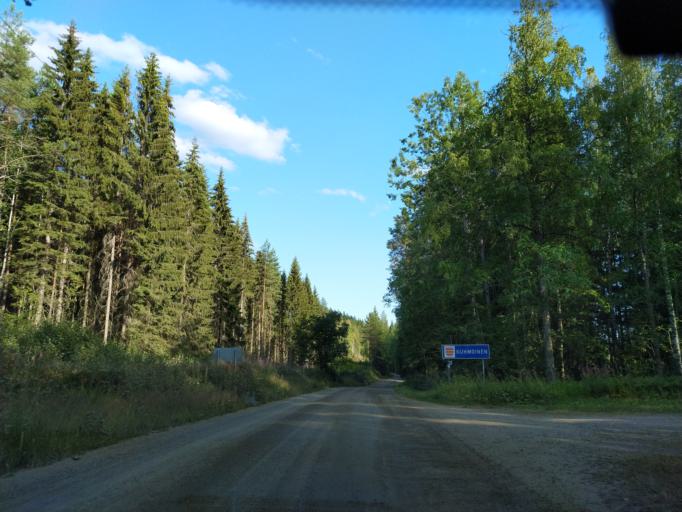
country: FI
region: Central Finland
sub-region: Jaemsae
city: Kuhmoinen
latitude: 61.7077
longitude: 24.9144
